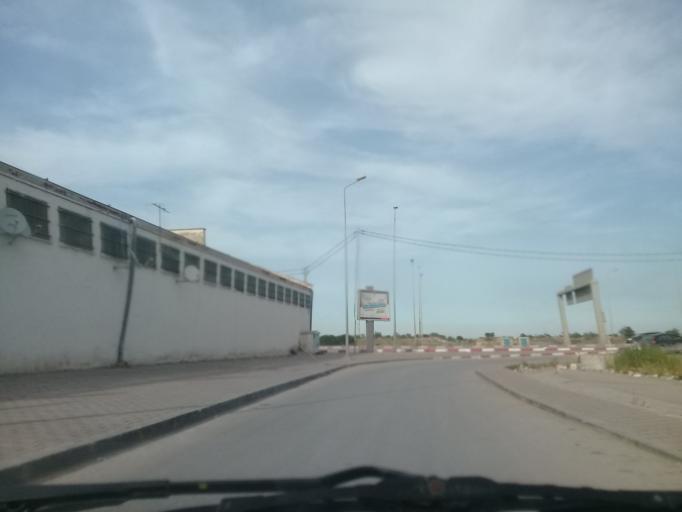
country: TN
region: Tunis
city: Tunis
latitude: 36.7933
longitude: 10.1896
